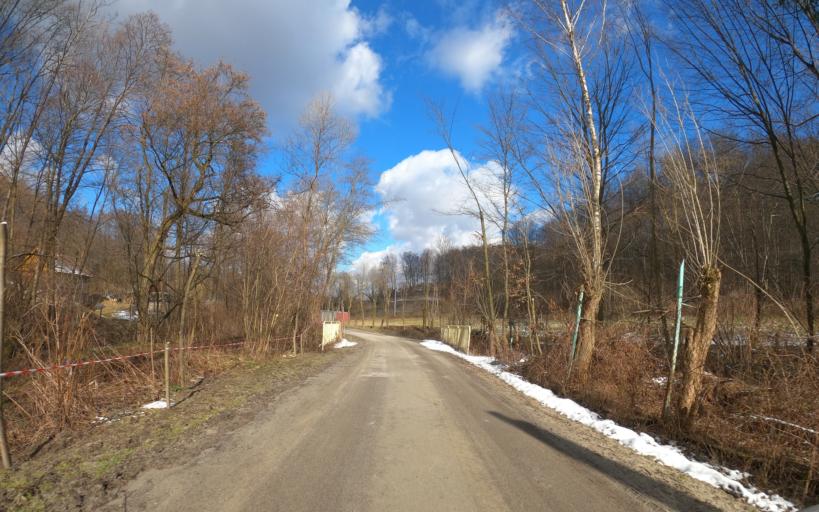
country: PL
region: Subcarpathian Voivodeship
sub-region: Powiat debicki
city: Debica
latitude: 50.0263
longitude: 21.4346
